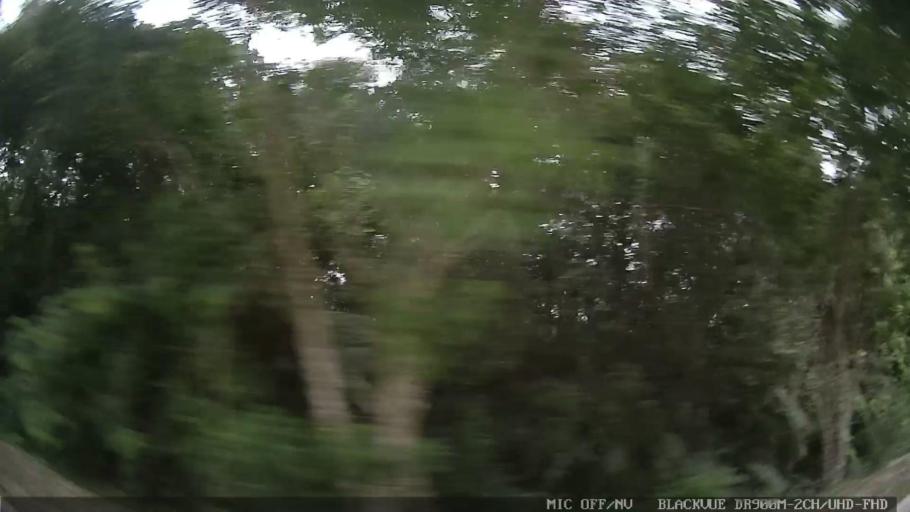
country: BR
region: Sao Paulo
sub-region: Itanhaem
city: Itanhaem
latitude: -24.1904
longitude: -46.8335
